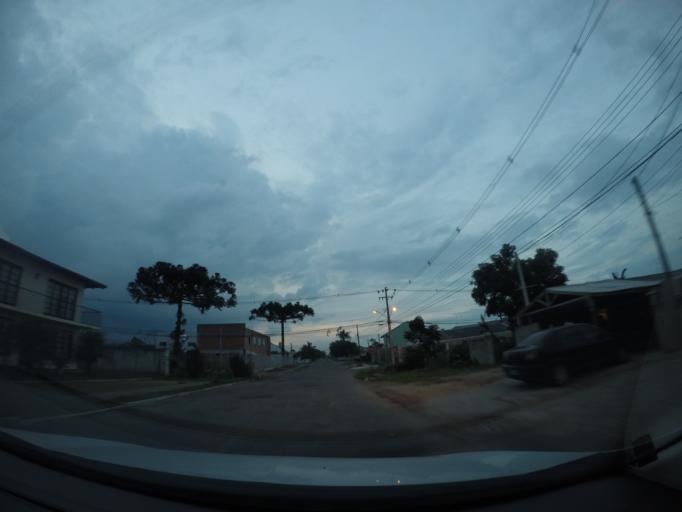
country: BR
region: Parana
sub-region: Sao Jose Dos Pinhais
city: Sao Jose dos Pinhais
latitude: -25.5005
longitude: -49.2297
